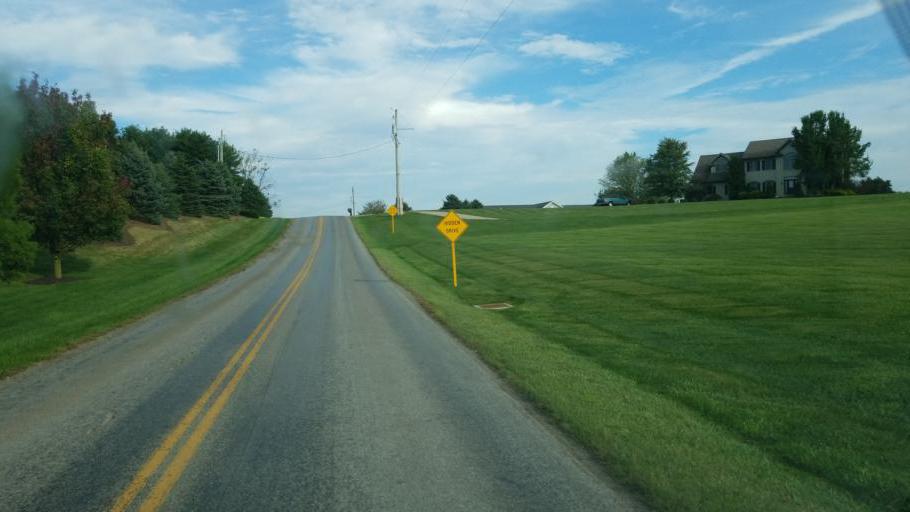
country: US
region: Ohio
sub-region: Holmes County
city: Millersburg
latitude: 40.5737
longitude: -81.8269
